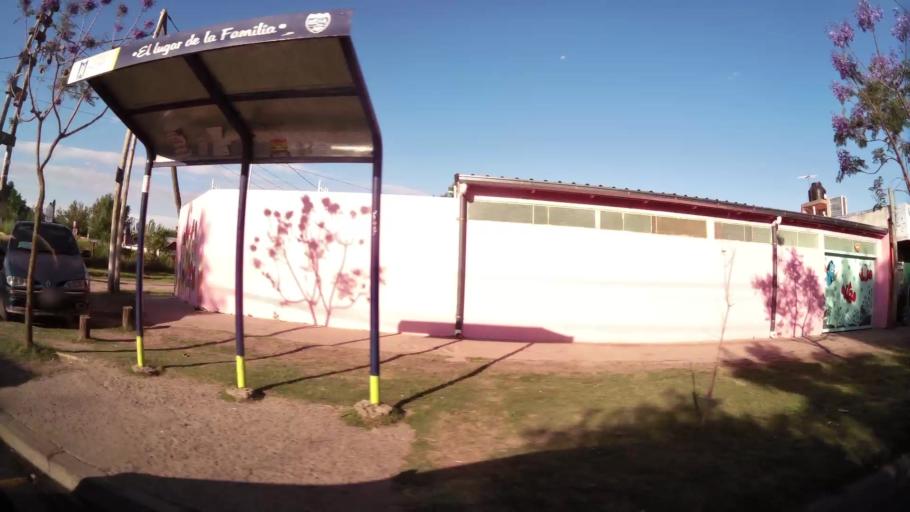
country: AR
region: Buenos Aires
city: Santa Catalina - Dique Lujan
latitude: -34.4679
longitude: -58.7409
